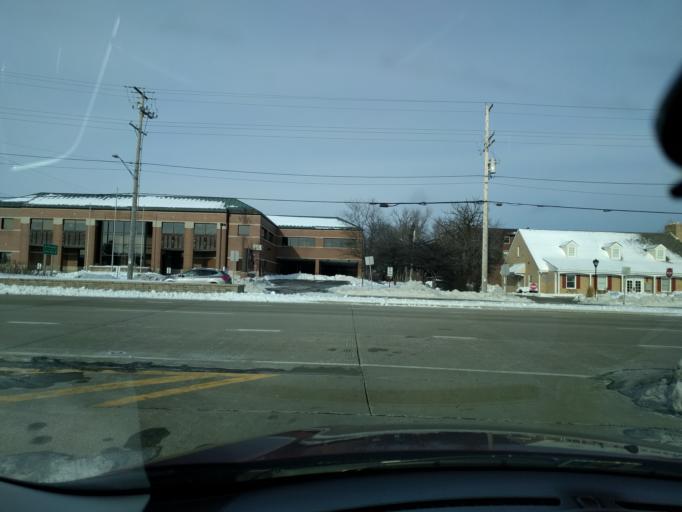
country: US
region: Wisconsin
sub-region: Milwaukee County
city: River Hills
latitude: 43.1766
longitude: -87.9143
